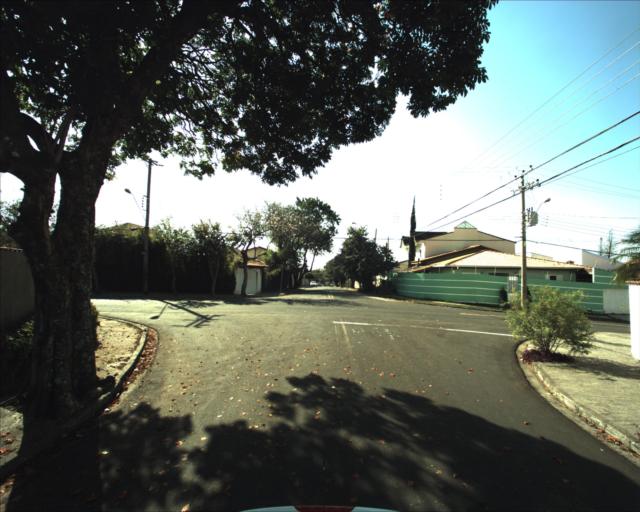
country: BR
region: Sao Paulo
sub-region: Sorocaba
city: Sorocaba
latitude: -23.4960
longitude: -47.4072
